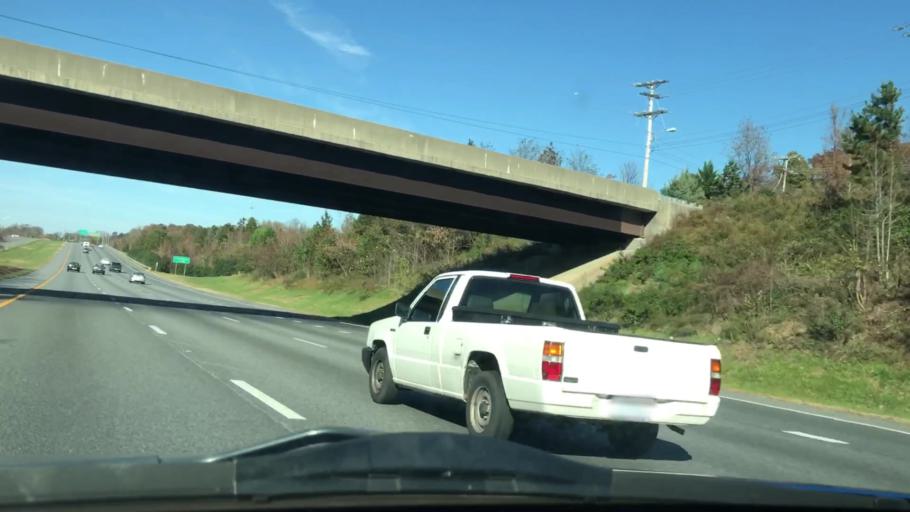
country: US
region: North Carolina
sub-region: Guilford County
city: High Point
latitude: 35.9732
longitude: -79.9743
